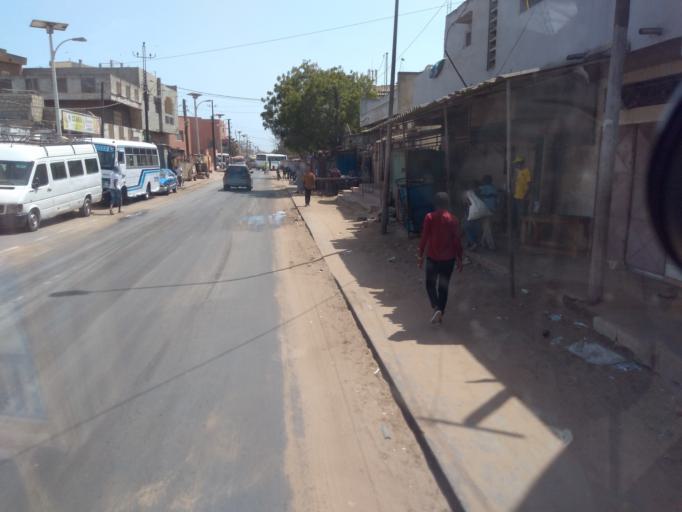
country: SN
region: Dakar
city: Pikine
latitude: 14.7676
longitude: -17.3669
